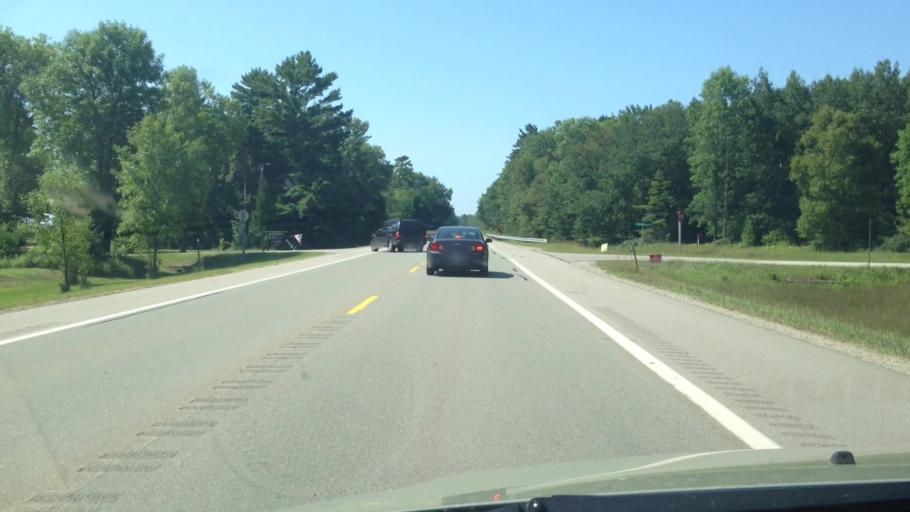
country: US
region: Michigan
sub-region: Menominee County
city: Menominee
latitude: 45.3213
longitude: -87.4304
